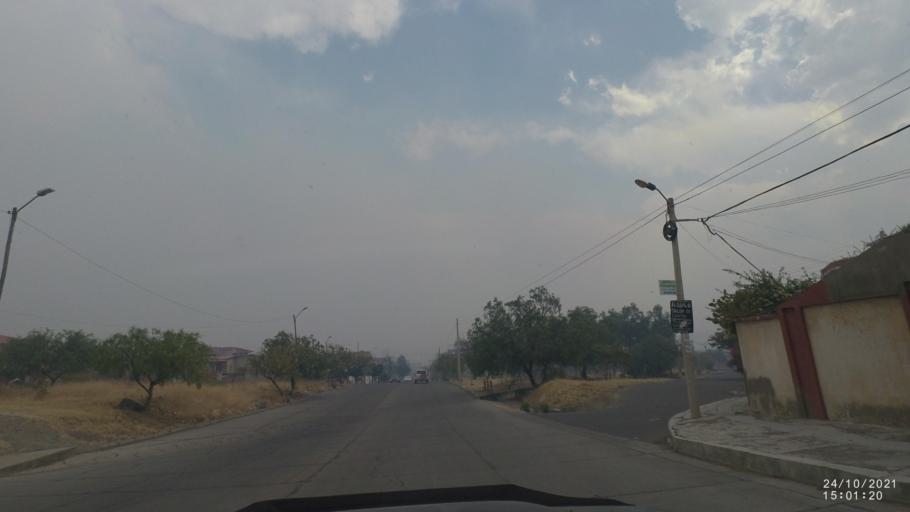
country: BO
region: Cochabamba
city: Cochabamba
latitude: -17.3612
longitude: -66.1547
